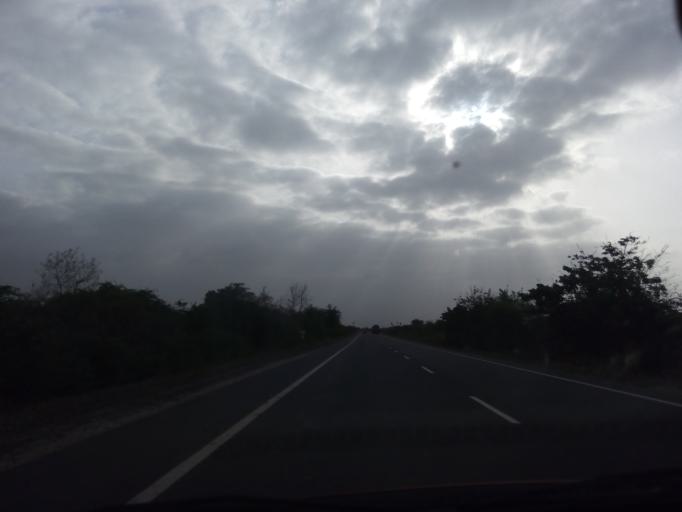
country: IN
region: Gujarat
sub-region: Kachchh
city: Anjar
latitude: 23.2833
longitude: 69.9951
